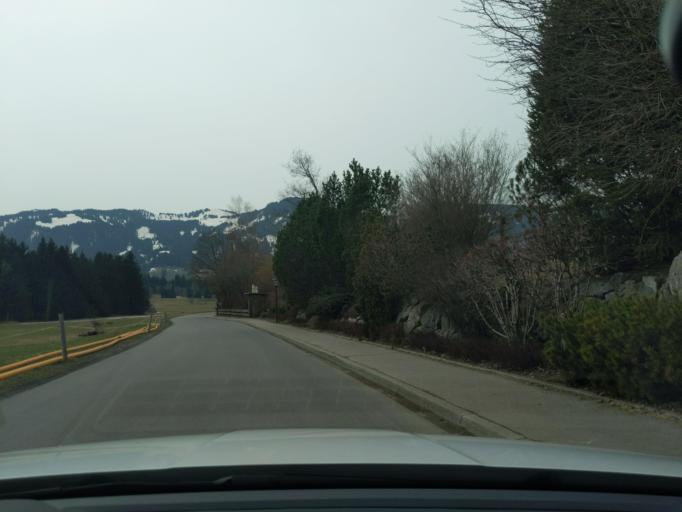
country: DE
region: Bavaria
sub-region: Swabia
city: Ofterschwang
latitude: 47.4891
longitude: 10.2582
